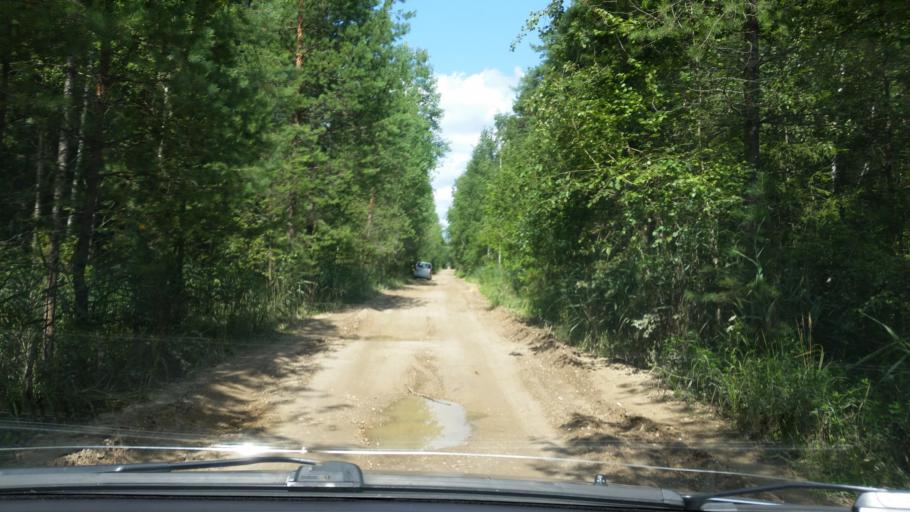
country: RU
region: Moskovskaya
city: Pushchino
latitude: 54.9066
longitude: 37.6857
